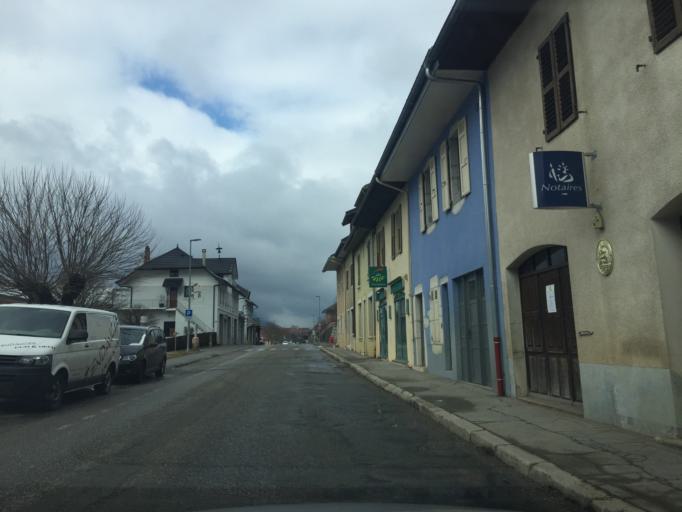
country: FR
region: Rhone-Alpes
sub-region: Departement de la Haute-Savoie
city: Doussard
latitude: 45.6860
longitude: 6.1362
